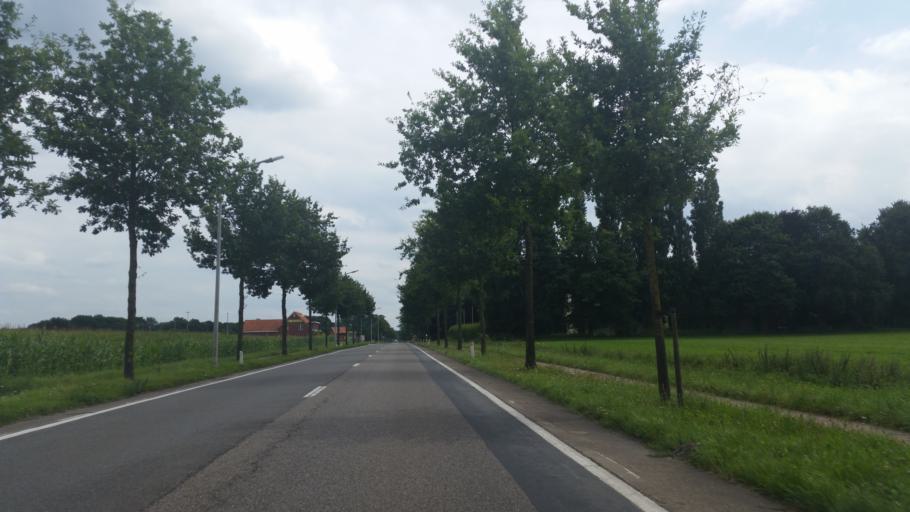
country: BE
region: Flanders
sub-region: Provincie Antwerpen
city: Merksplas
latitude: 51.3428
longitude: 4.8945
